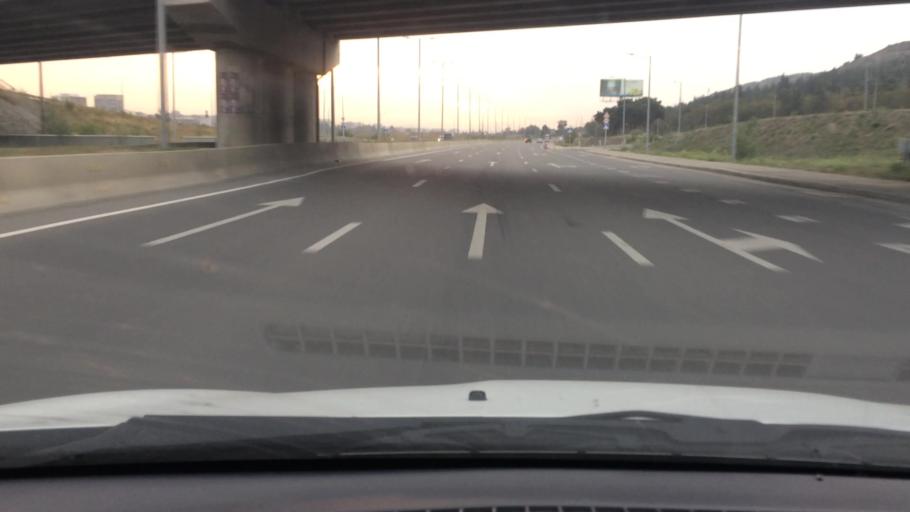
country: GE
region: T'bilisi
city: Tbilisi
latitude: 41.6692
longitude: 44.8576
